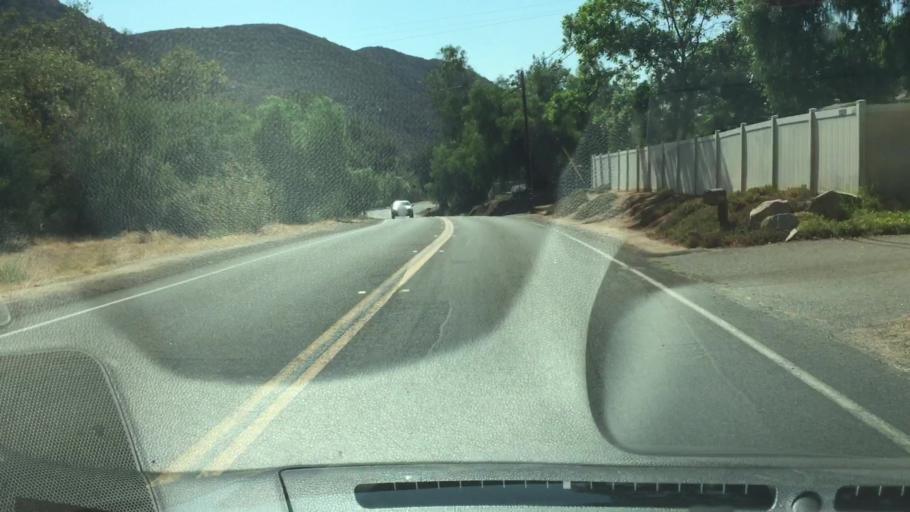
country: US
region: California
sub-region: San Diego County
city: Jamul
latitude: 32.7345
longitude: -116.8866
